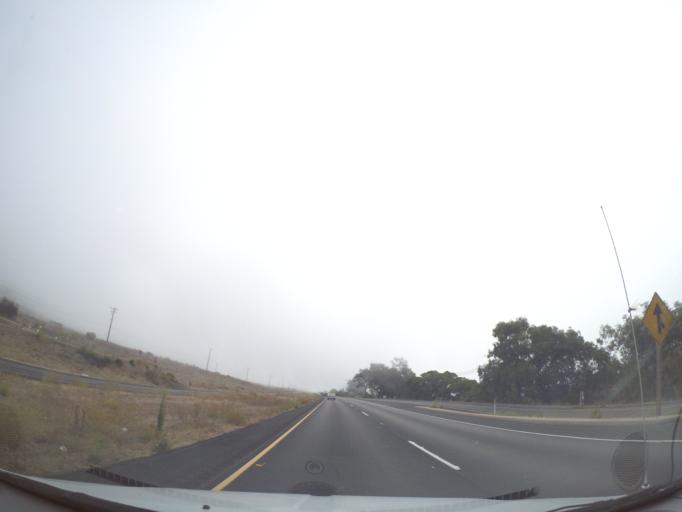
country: US
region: California
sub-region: Santa Barbara County
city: Santa Ynez
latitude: 34.4628
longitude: -120.0189
